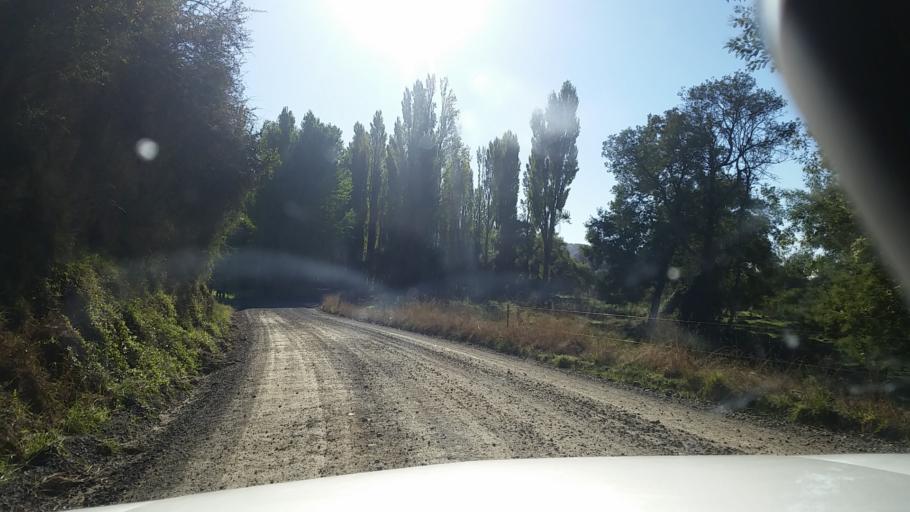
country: NZ
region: Marlborough
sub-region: Marlborough District
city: Blenheim
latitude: -41.4455
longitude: 173.8947
